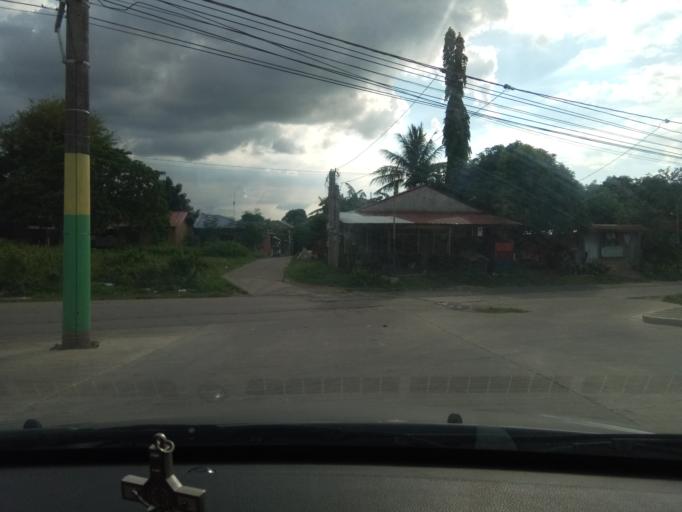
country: PH
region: Calabarzon
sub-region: Province of Cavite
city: Biga
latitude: 14.2811
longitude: 120.9469
